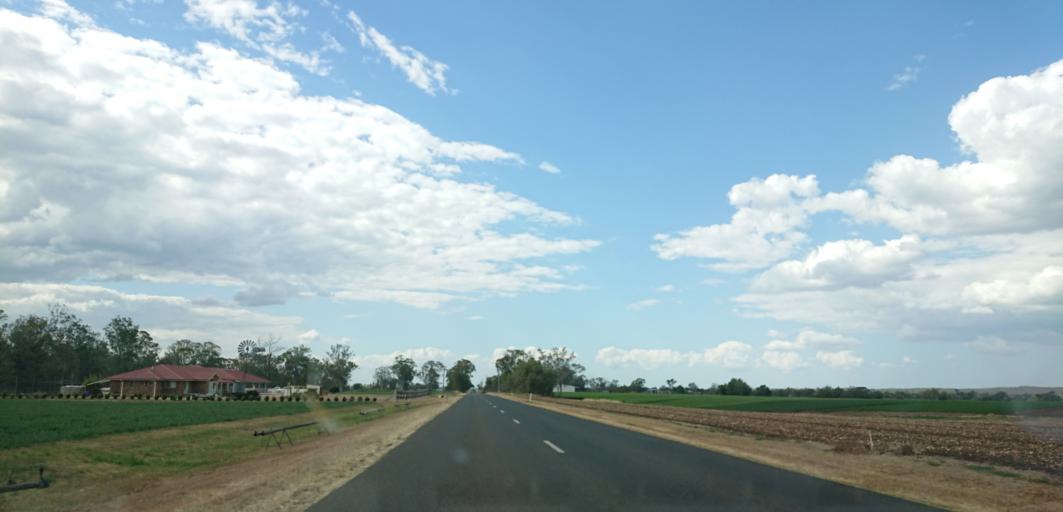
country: AU
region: Queensland
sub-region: Lockyer Valley
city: Gatton
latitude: -27.6028
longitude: 152.2156
